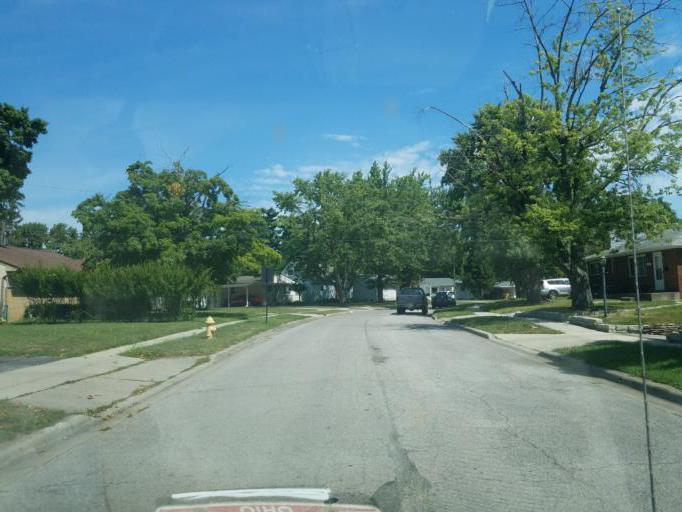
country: US
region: Ohio
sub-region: Franklin County
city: Grove City
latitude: 39.8790
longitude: -83.0809
